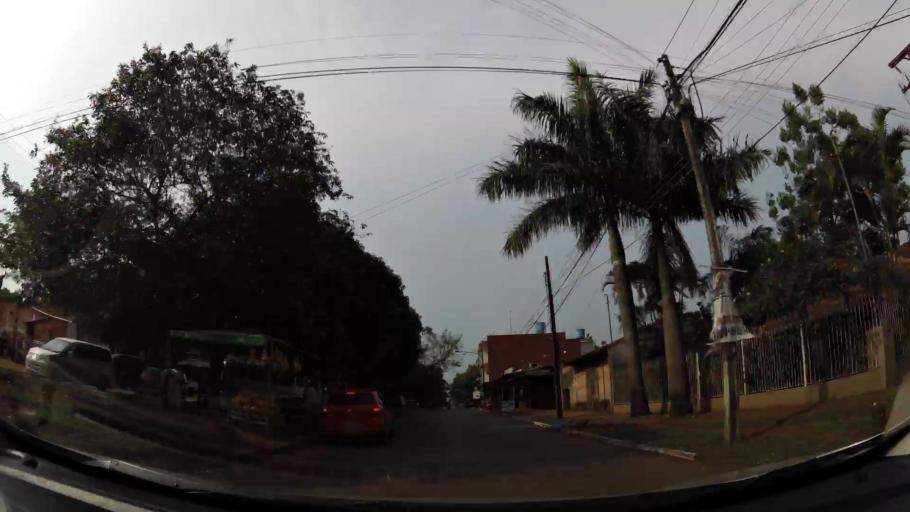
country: PY
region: Alto Parana
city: Ciudad del Este
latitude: -25.4997
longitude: -54.6516
